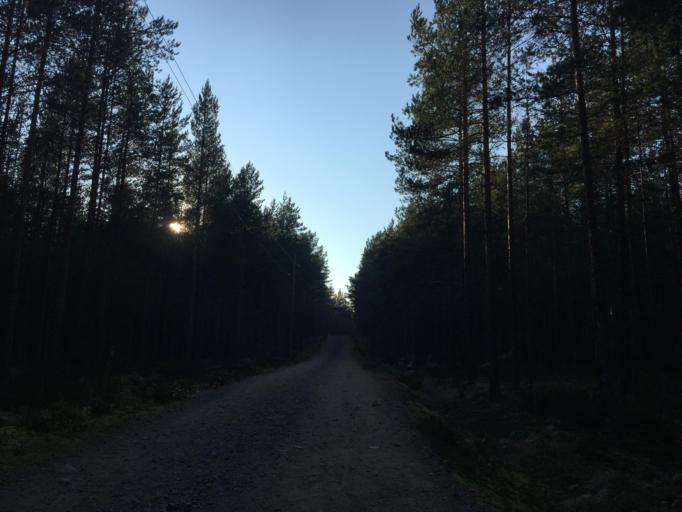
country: RU
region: Leningrad
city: Priozersk
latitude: 61.2842
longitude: 30.1236
